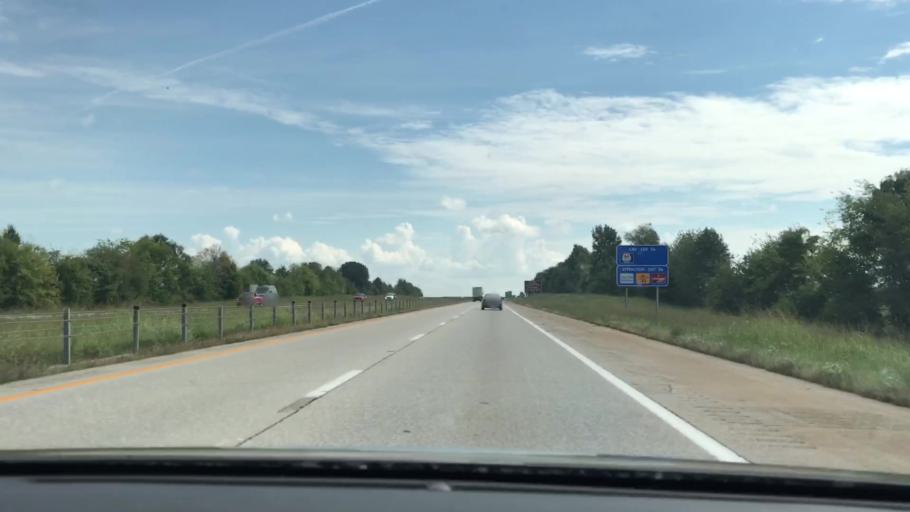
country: US
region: Kentucky
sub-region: Trigg County
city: Cadiz
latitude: 36.9711
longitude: -87.8866
